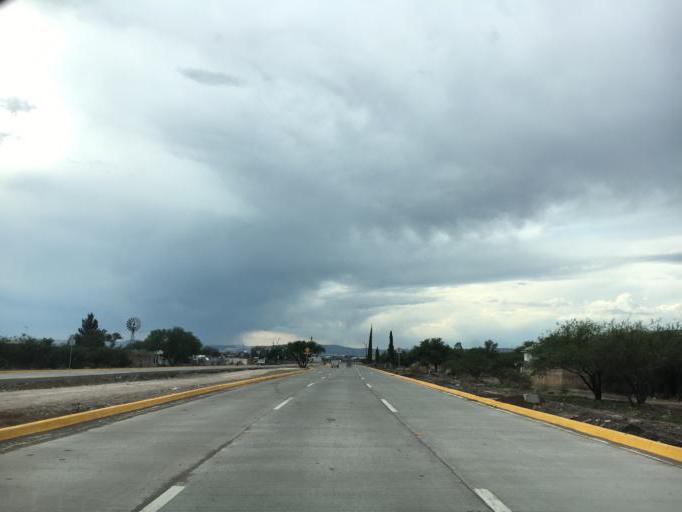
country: MX
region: Guanajuato
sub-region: Leon
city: Fraccionamiento Paraiso Real
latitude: 21.1085
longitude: -101.5827
